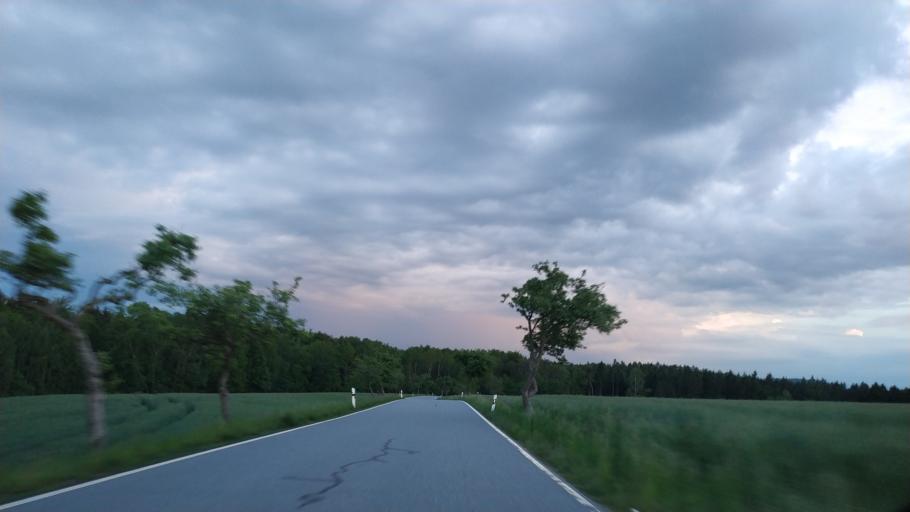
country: DE
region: Saxony
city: Hohnstein
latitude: 50.9786
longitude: 14.0904
